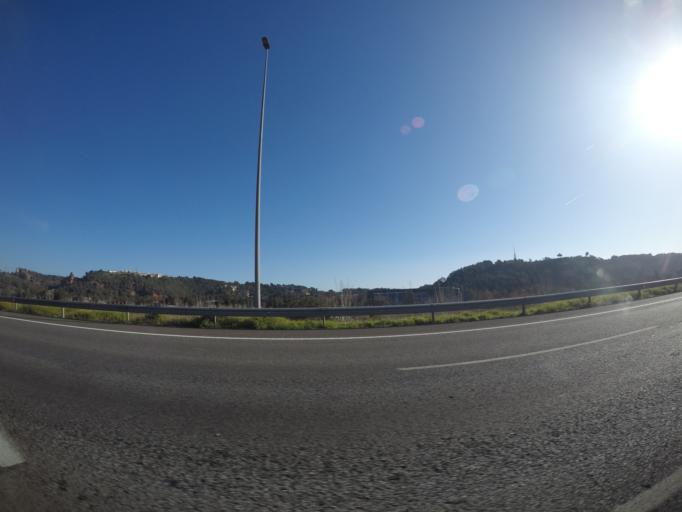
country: ES
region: Catalonia
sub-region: Provincia de Barcelona
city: Sant Andreu de la Barca
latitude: 41.4622
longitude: 1.9728
